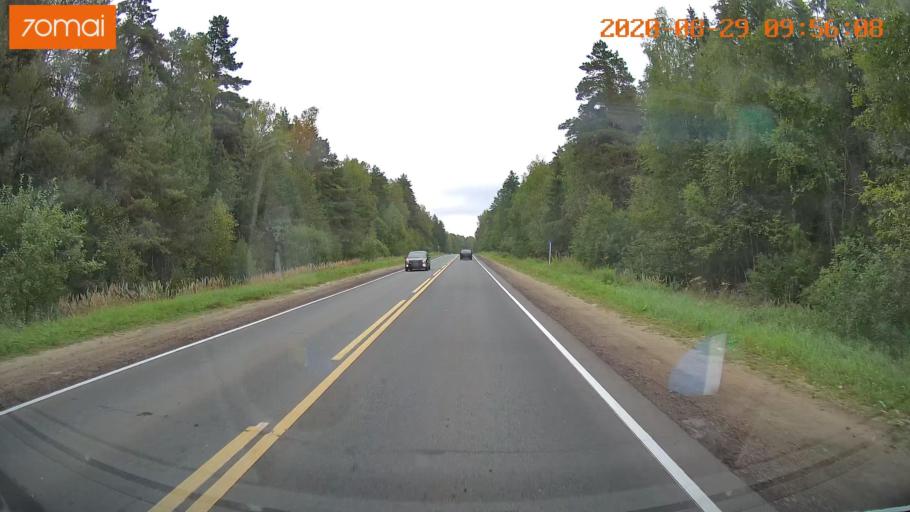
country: RU
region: Ivanovo
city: Zarechnyy
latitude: 57.4212
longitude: 42.2815
